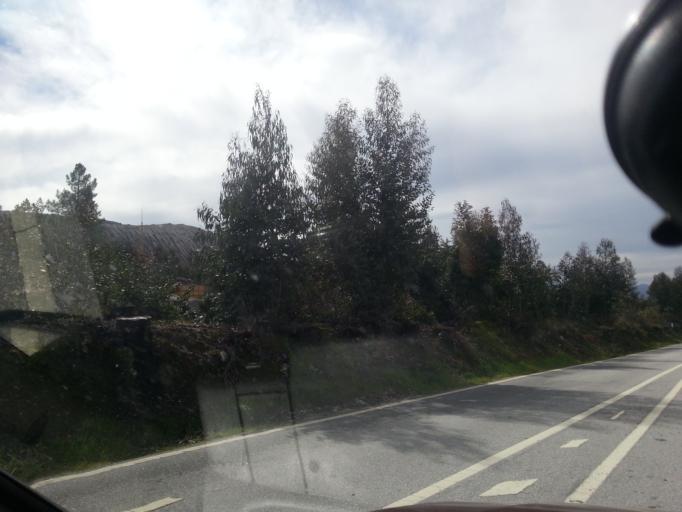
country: PT
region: Guarda
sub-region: Fornos de Algodres
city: Fornos de Algodres
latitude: 40.5959
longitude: -7.5325
